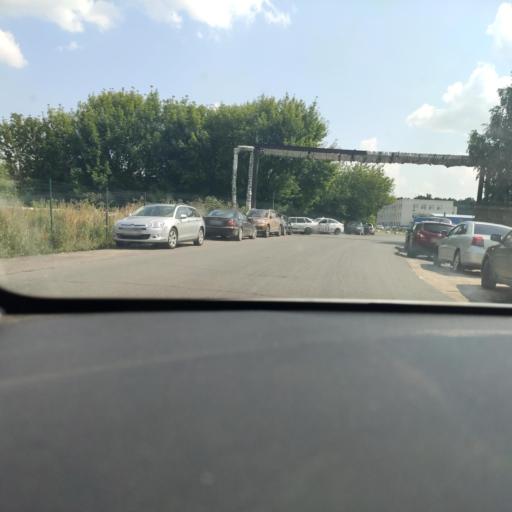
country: RU
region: Tatarstan
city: Stolbishchi
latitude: 55.6154
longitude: 49.2815
